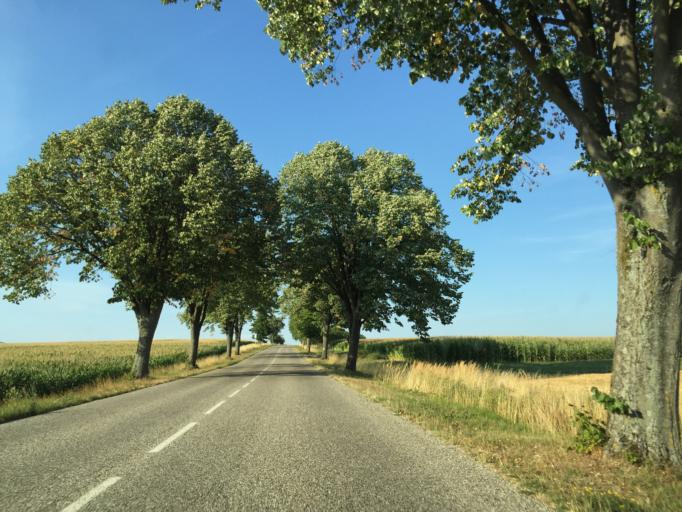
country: FR
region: Alsace
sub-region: Departement du Bas-Rhin
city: Surbourg
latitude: 48.9210
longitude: 7.8635
